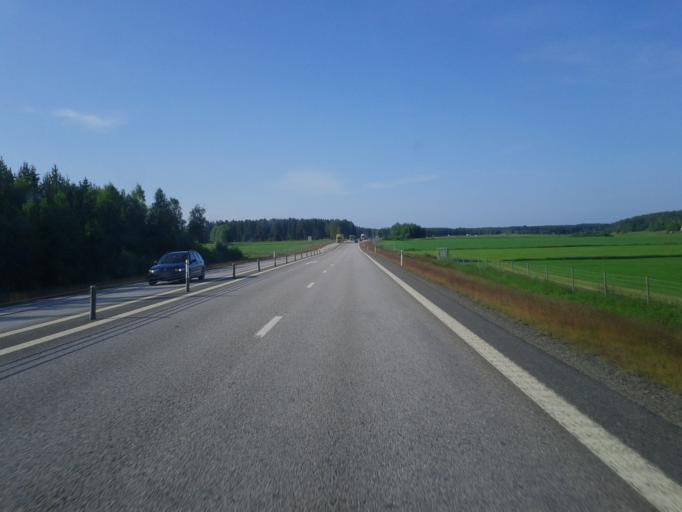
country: SE
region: Vaesterbotten
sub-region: Robertsfors Kommun
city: Robertsfors
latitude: 64.0954
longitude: 20.8695
